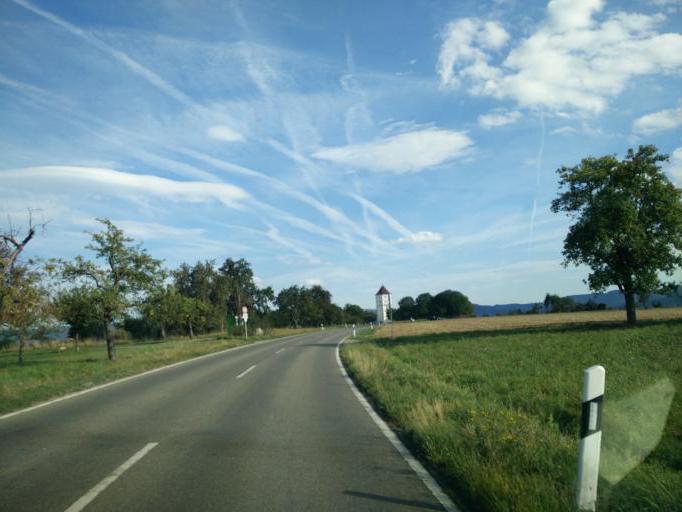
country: DE
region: Baden-Wuerttemberg
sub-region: Tuebingen Region
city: Kirchentellinsfurt
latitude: 48.5280
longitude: 9.1638
